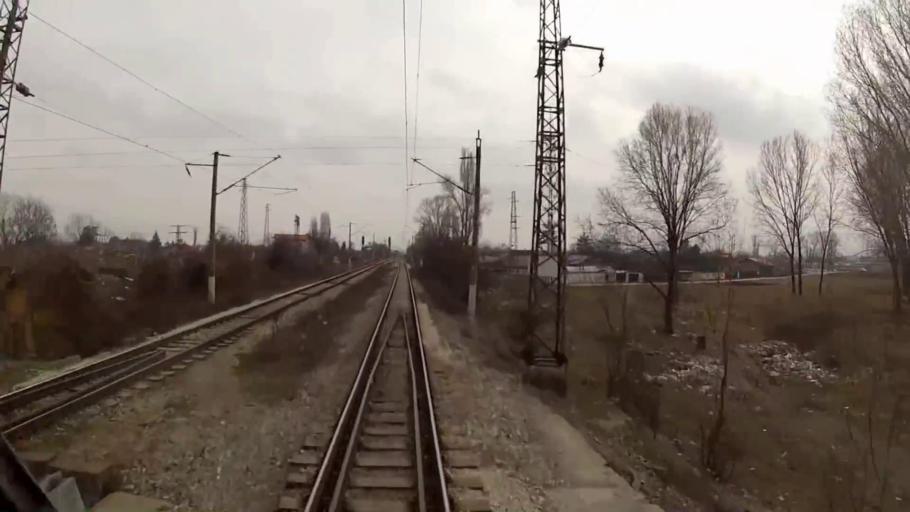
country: BG
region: Sofiya
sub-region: Obshtina Elin Pelin
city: Elin Pelin
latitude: 42.6528
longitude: 23.4670
